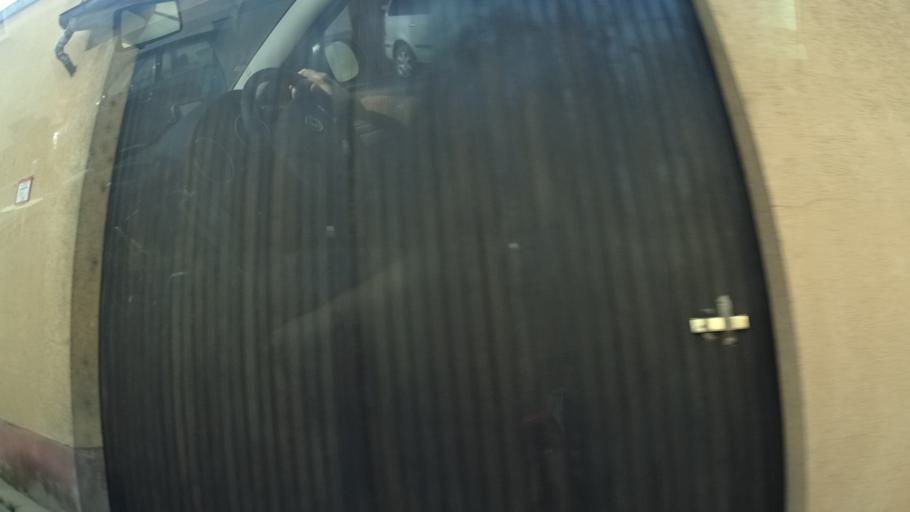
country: DE
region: Bavaria
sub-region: Regierungsbezirk Unterfranken
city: Zellingen
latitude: 49.8667
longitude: 9.7998
